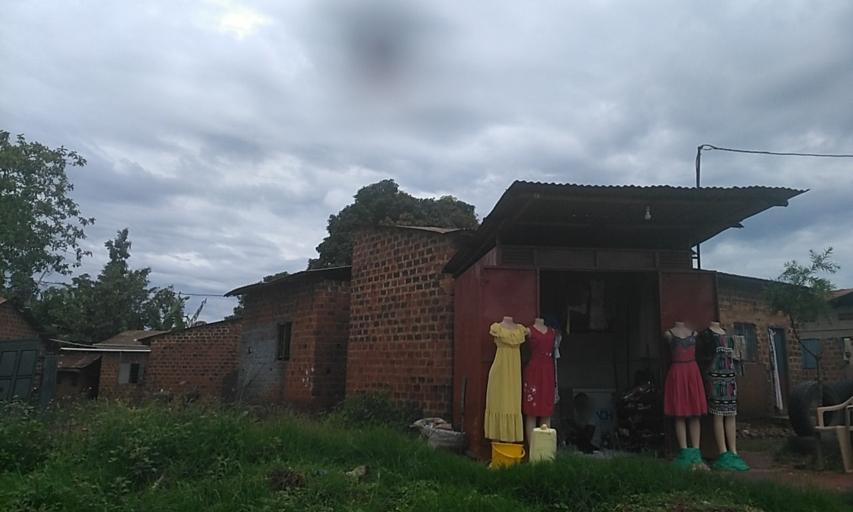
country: UG
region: Central Region
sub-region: Wakiso District
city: Bweyogerere
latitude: 0.3964
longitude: 32.7009
